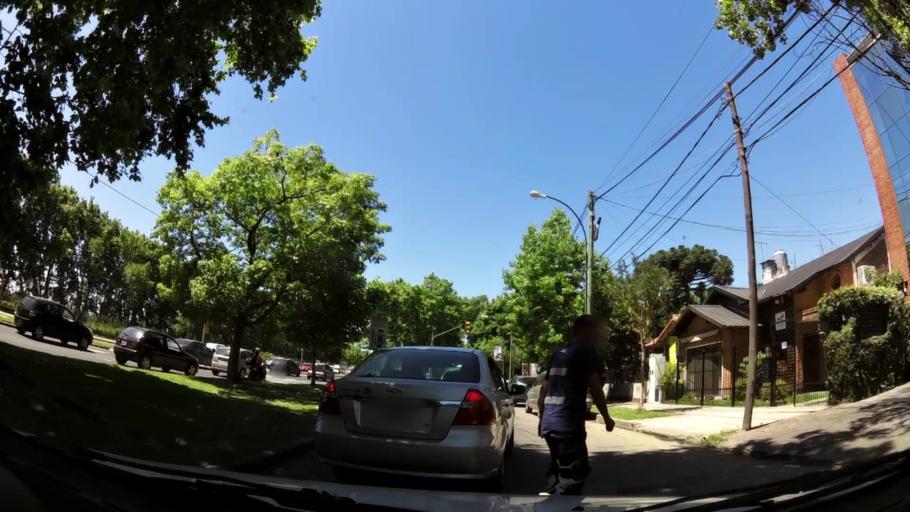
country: AR
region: Buenos Aires
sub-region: Partido de San Isidro
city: San Isidro
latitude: -34.4957
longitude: -58.5361
